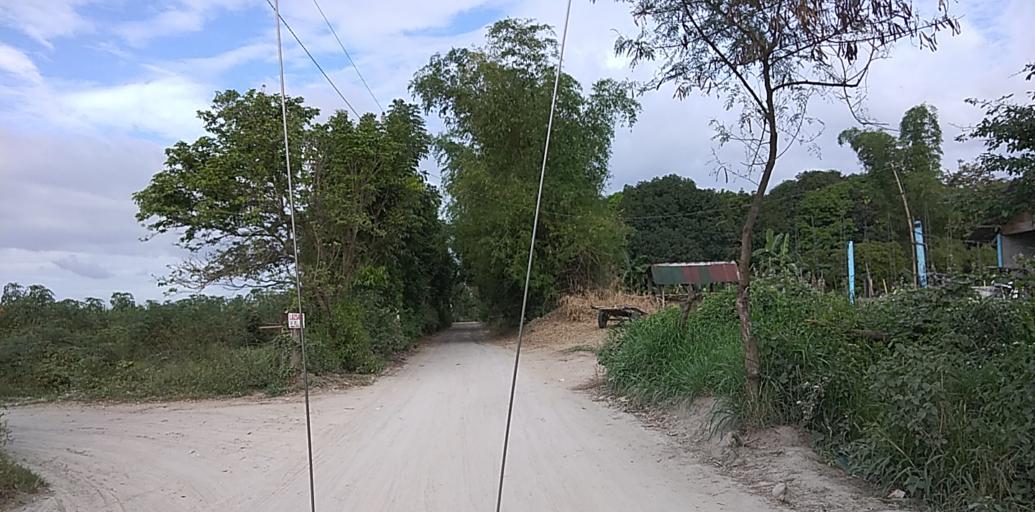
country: PH
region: Central Luzon
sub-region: Province of Pampanga
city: Pulung Santol
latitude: 15.0556
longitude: 120.5636
